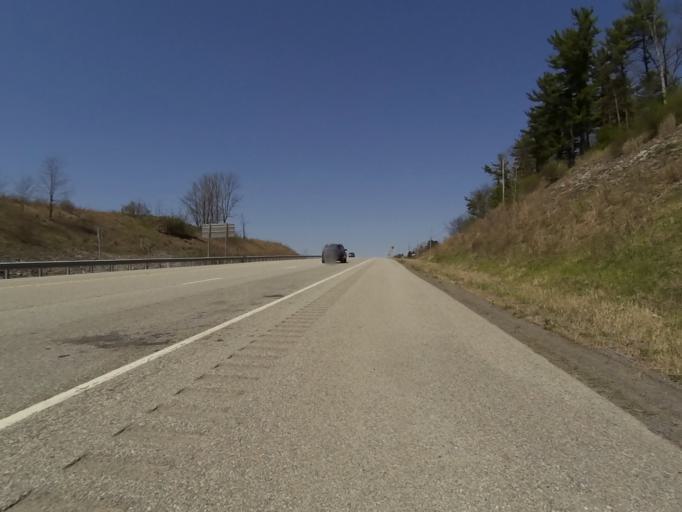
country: US
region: Pennsylvania
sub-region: Blair County
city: Williamsburg
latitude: 40.5772
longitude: -78.1418
